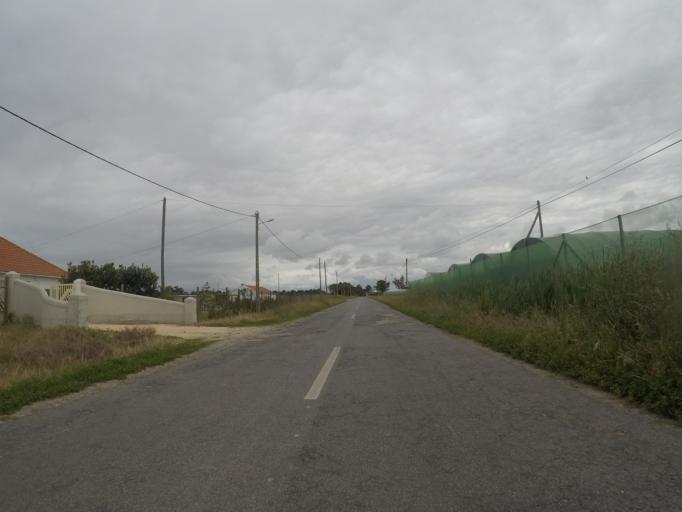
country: PT
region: Beja
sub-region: Odemira
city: Vila Nova de Milfontes
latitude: 37.6044
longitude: -8.8007
